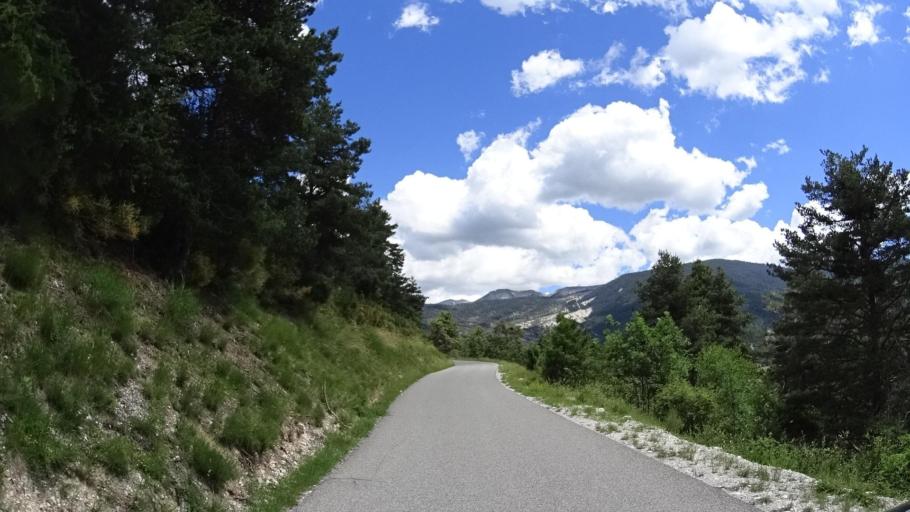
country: FR
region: Provence-Alpes-Cote d'Azur
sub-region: Departement des Alpes-de-Haute-Provence
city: Annot
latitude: 44.0213
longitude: 6.6192
